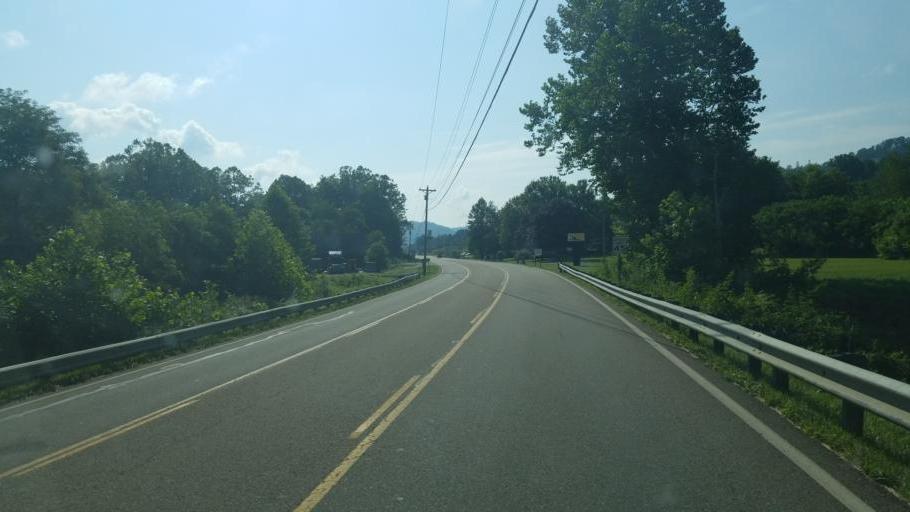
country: US
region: Tennessee
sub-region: Carter County
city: Roan Mountain
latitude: 36.1954
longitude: -82.0635
